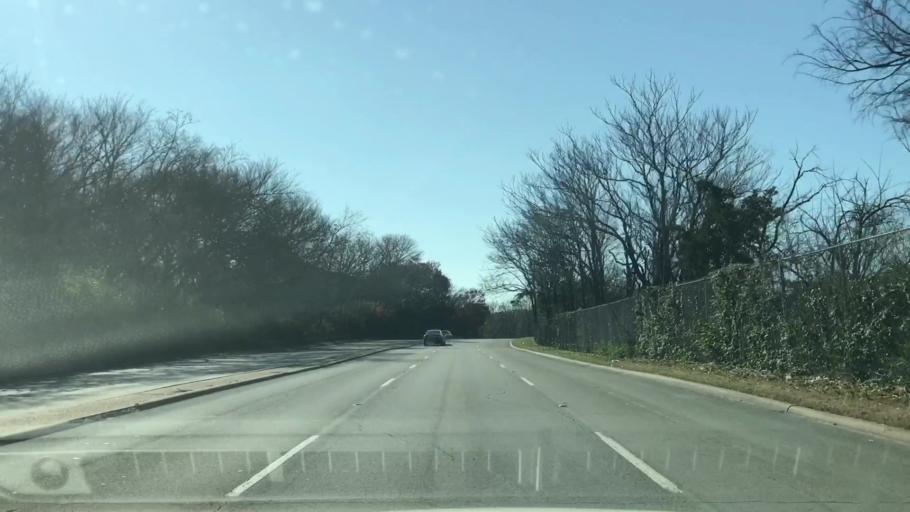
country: US
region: Texas
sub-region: Dallas County
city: Dallas
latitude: 32.7377
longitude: -96.8133
